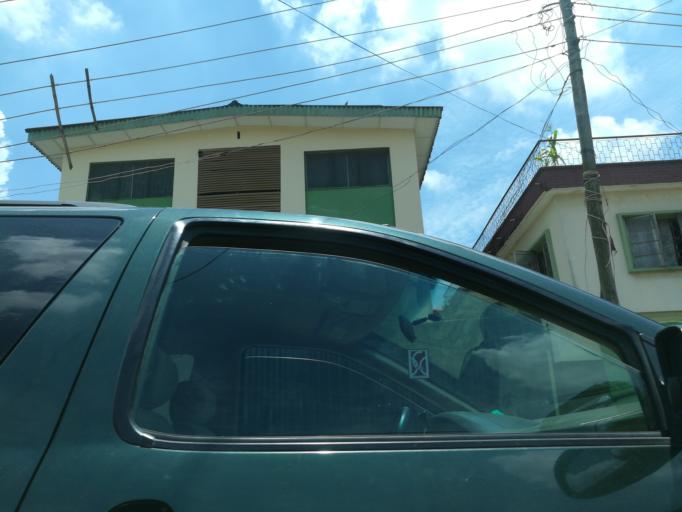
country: NG
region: Lagos
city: Ikorodu
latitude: 6.6174
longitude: 3.5019
